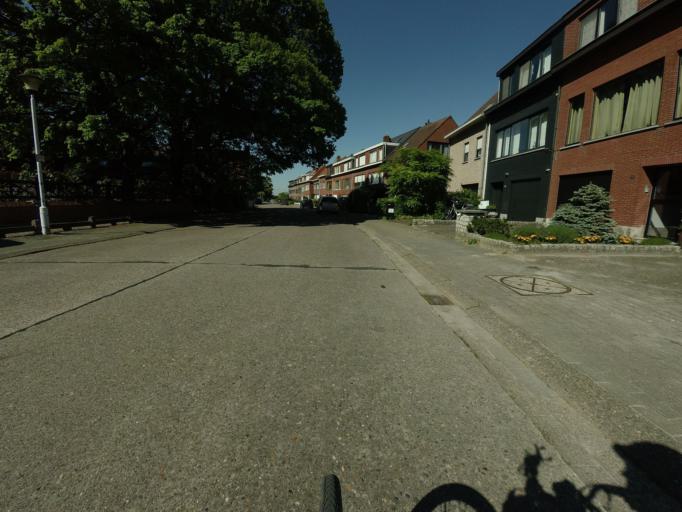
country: BE
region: Flanders
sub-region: Provincie Antwerpen
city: Boechout
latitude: 51.1686
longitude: 4.4970
